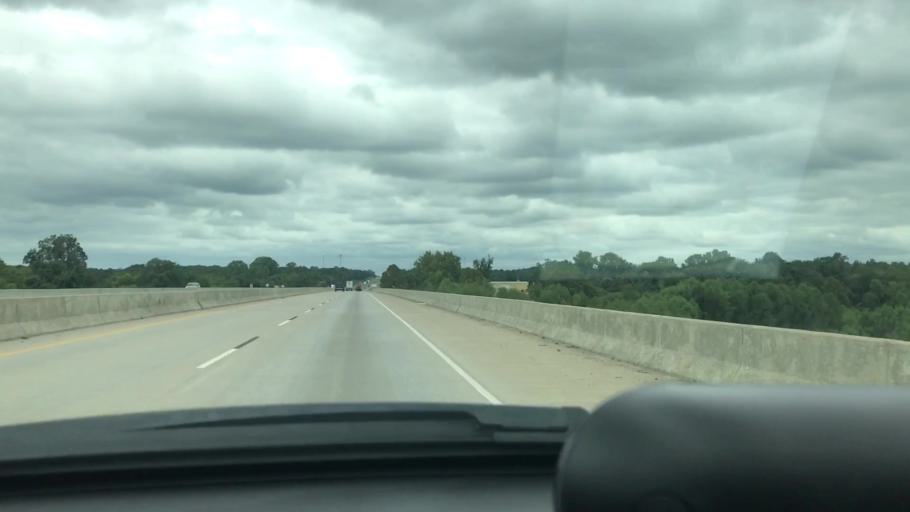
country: US
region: Oklahoma
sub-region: Muskogee County
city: Muskogee
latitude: 35.8086
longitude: -95.4021
